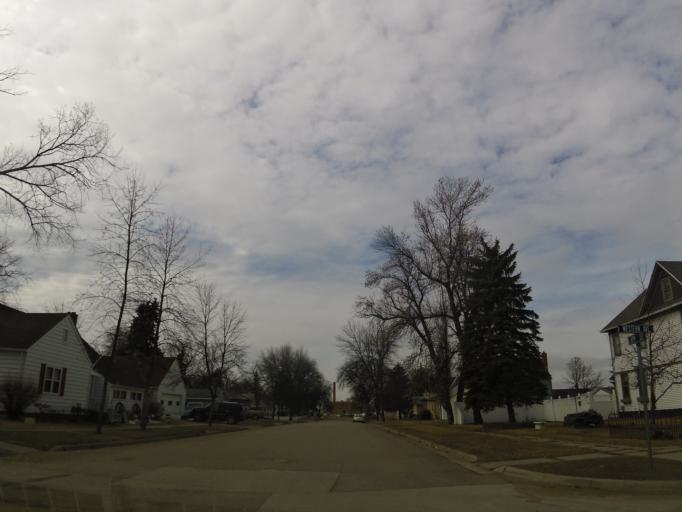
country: US
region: North Dakota
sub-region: Walsh County
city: Grafton
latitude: 48.4186
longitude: -97.4156
